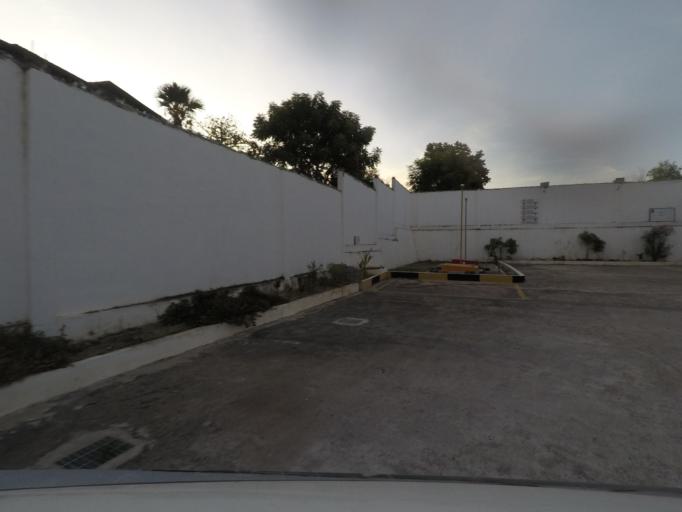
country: TL
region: Baucau
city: Baucau
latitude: -8.4726
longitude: 126.5983
